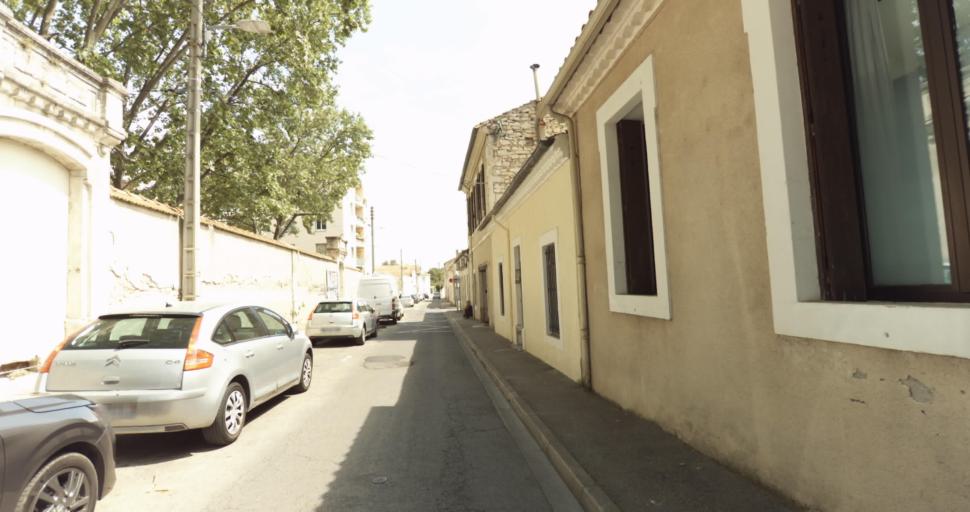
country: FR
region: Languedoc-Roussillon
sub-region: Departement du Gard
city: Nimes
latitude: 43.8473
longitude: 4.3642
